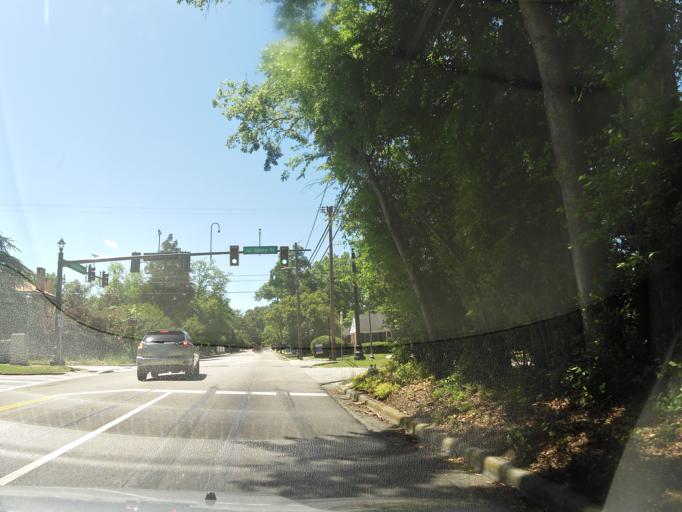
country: US
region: Georgia
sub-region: Richmond County
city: Augusta
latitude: 33.4809
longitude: -82.0312
